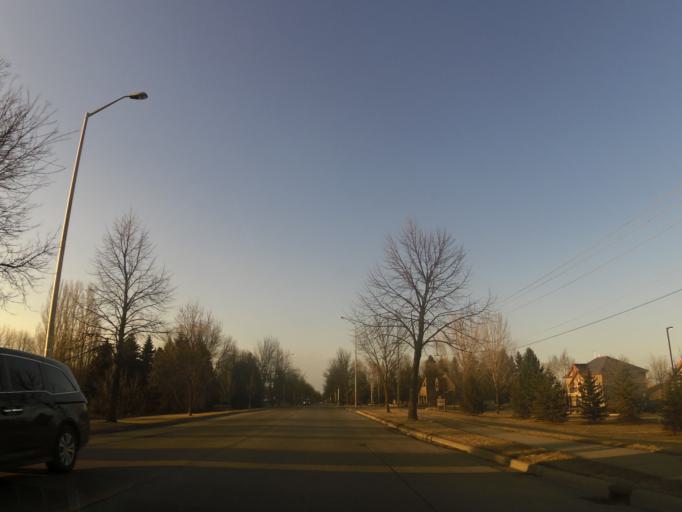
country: US
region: North Dakota
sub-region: Grand Forks County
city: Grand Forks
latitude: 47.8830
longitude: -97.0291
